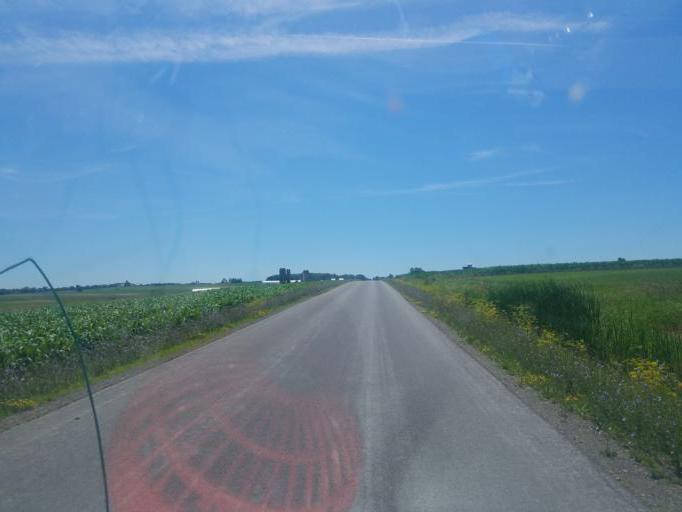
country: US
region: New York
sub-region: Yates County
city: Penn Yan
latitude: 42.6489
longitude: -77.0177
